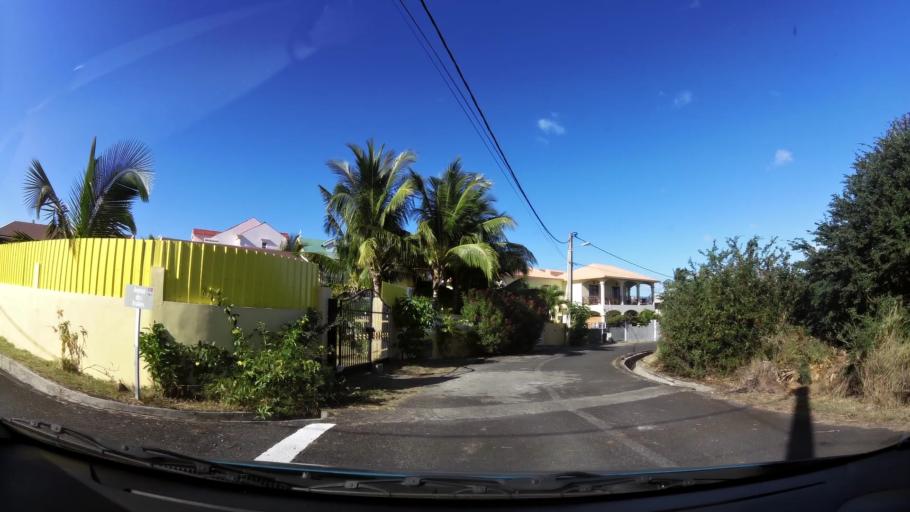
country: MU
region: Black River
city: Grande Riviere Noire
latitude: -20.3552
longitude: 57.3646
